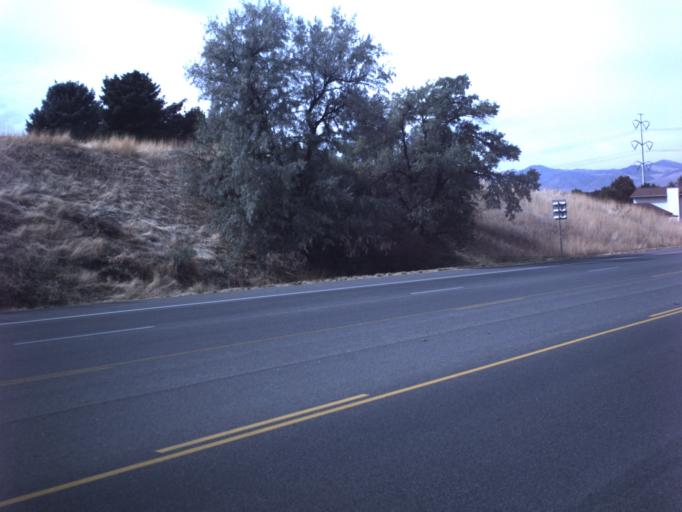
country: US
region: Utah
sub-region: Salt Lake County
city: Taylorsville
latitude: 40.6531
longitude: -111.9146
